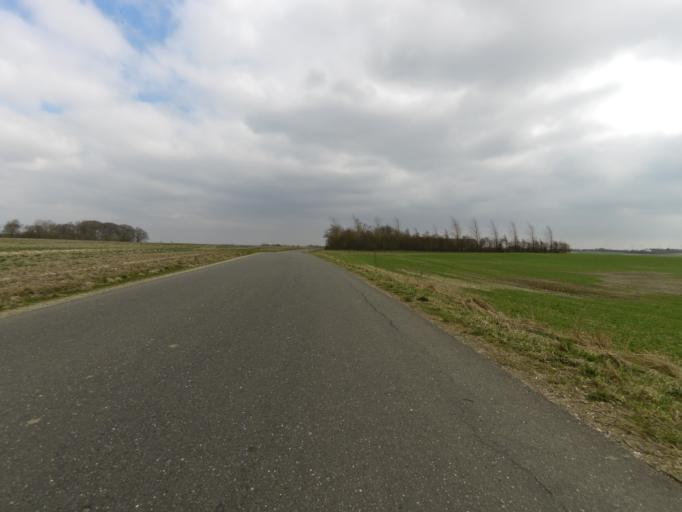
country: DK
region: Central Jutland
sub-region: Holstebro Kommune
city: Holstebro
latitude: 56.4259
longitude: 8.6910
